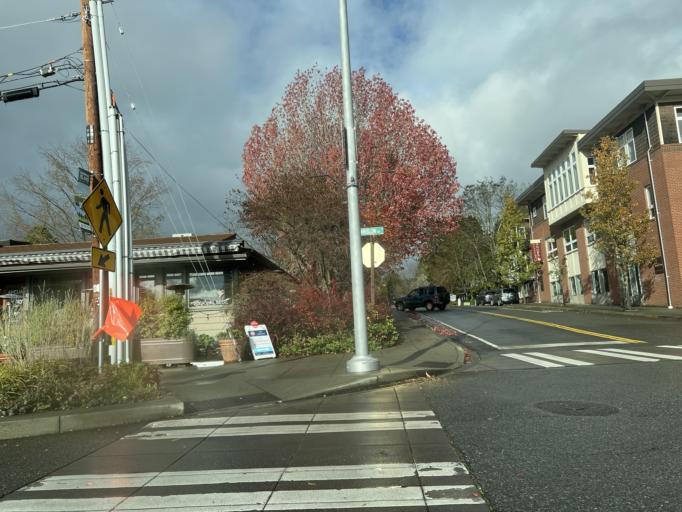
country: US
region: Washington
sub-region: Kitsap County
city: Bainbridge Island
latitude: 47.6248
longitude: -122.5171
